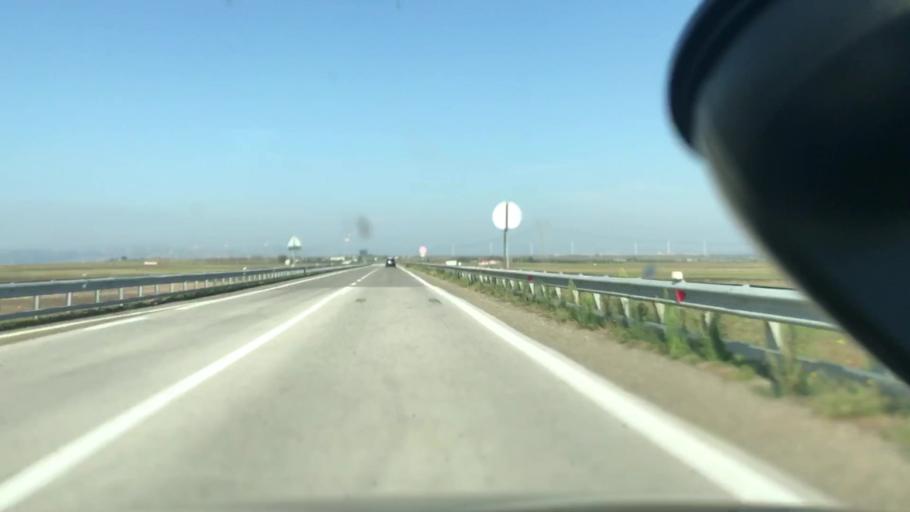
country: IT
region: Basilicate
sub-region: Provincia di Potenza
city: Venosa
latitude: 40.9947
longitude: 15.8846
